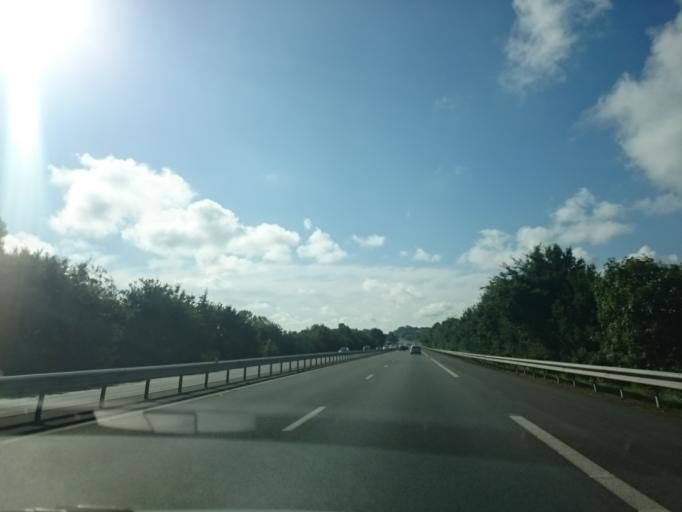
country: FR
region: Brittany
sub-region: Departement des Cotes-d'Armor
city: Broons
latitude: 48.3318
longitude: -2.2648
